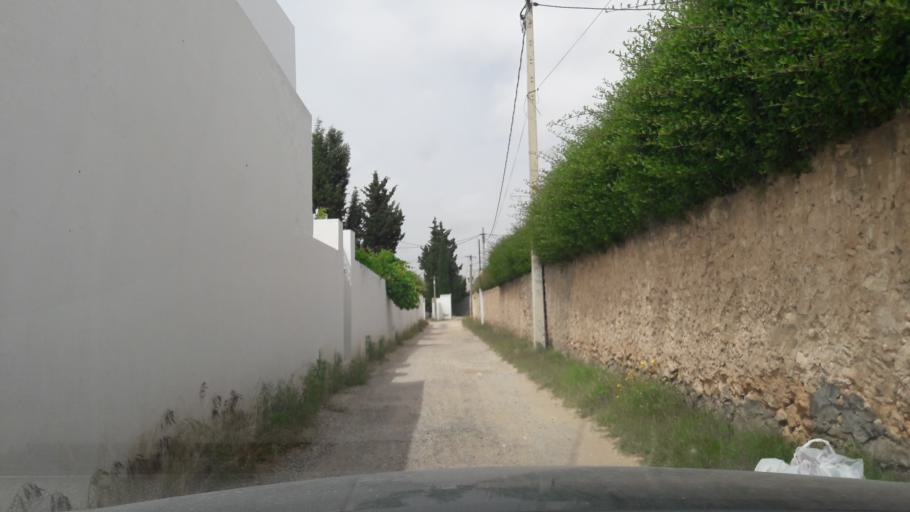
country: TN
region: Safaqis
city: Al Qarmadah
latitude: 34.7943
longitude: 10.7603
